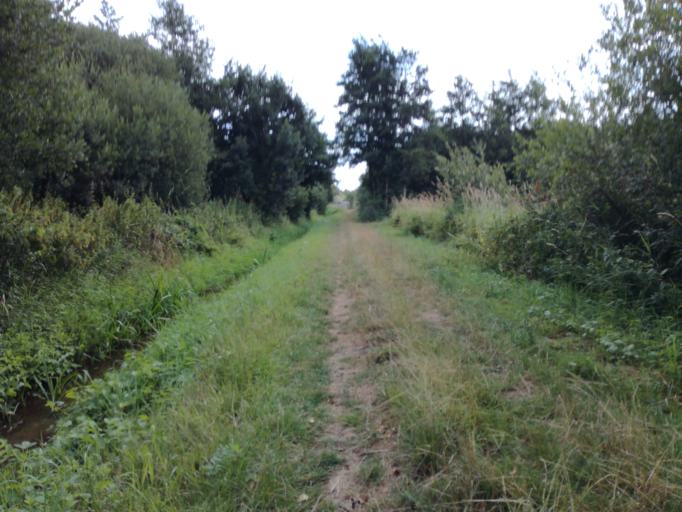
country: DK
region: South Denmark
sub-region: Vejle Kommune
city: Brejning
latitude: 55.6310
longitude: 9.7344
